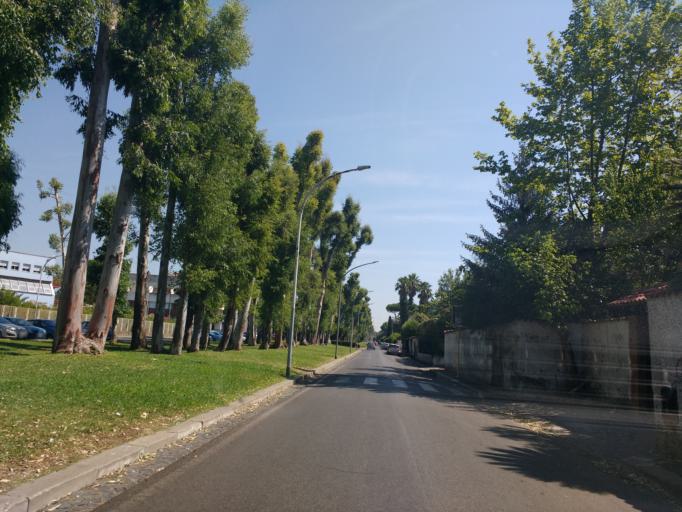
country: IT
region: Latium
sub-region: Citta metropolitana di Roma Capitale
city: Acilia-Castel Fusano-Ostia Antica
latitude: 41.7519
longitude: 12.3572
